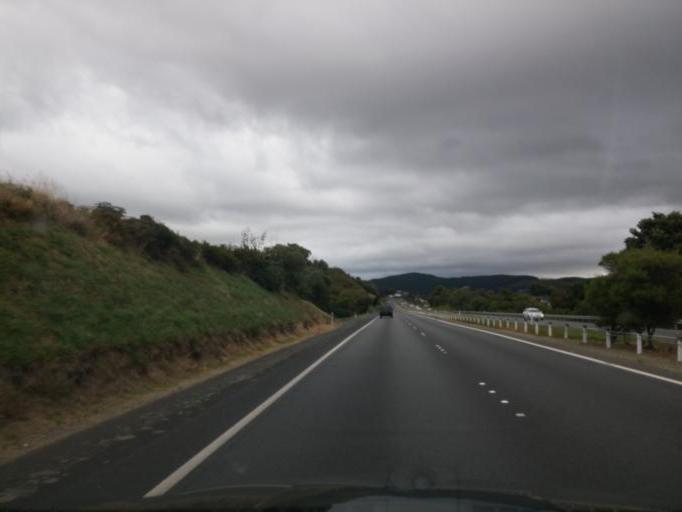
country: NZ
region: Wellington
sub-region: Porirua City
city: Porirua
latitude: -41.1605
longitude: 174.8363
